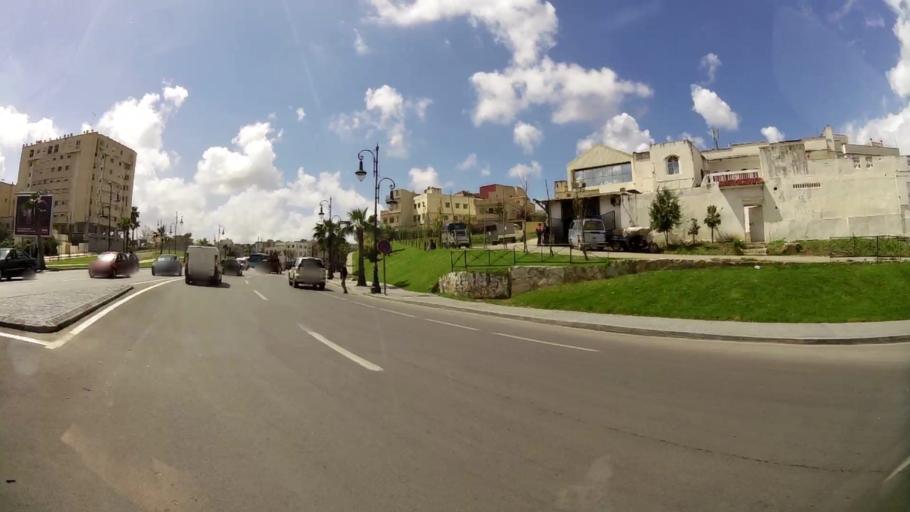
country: MA
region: Tanger-Tetouan
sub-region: Tanger-Assilah
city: Tangier
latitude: 35.7516
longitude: -5.8340
